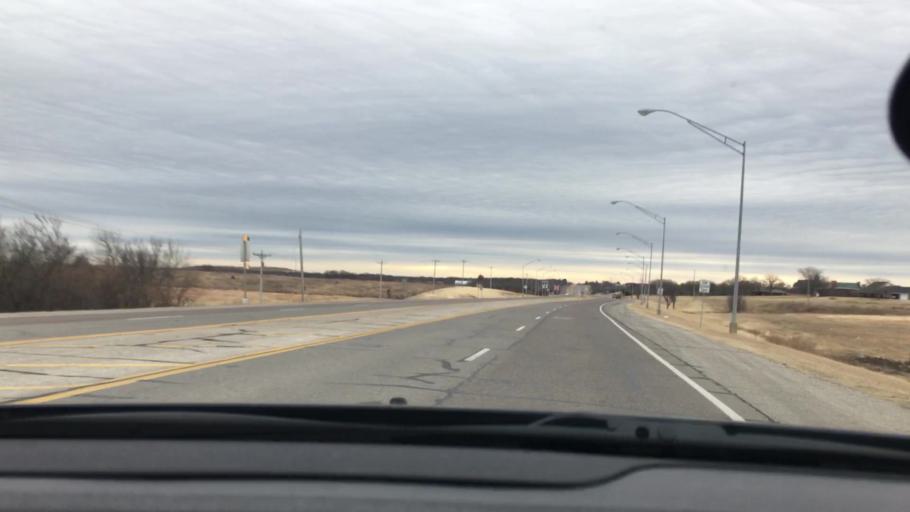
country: US
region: Oklahoma
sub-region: Carter County
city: Ardmore
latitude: 34.1872
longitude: -97.0812
